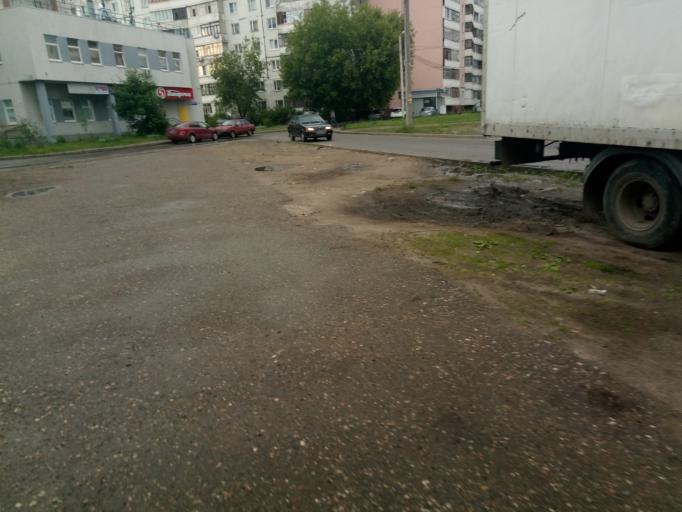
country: RU
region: Jaroslavl
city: Yaroslavl
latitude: 57.6506
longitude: 39.9590
